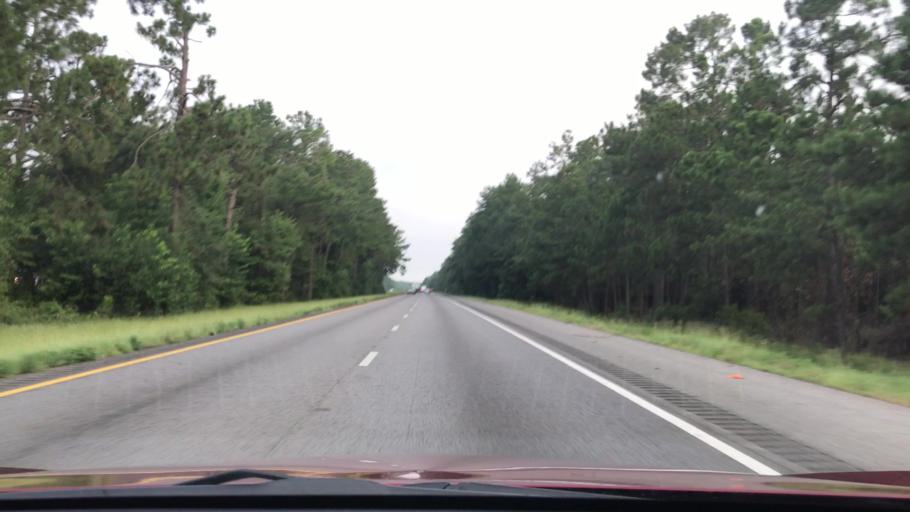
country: US
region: South Carolina
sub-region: Dorchester County
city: Ridgeville
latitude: 33.1732
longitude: -80.3678
